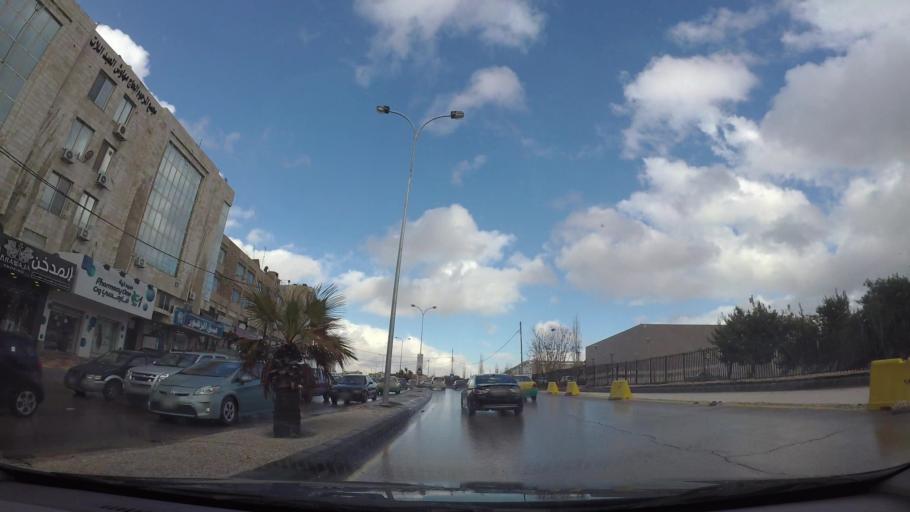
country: JO
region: Amman
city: Amman
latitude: 31.9872
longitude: 35.9046
